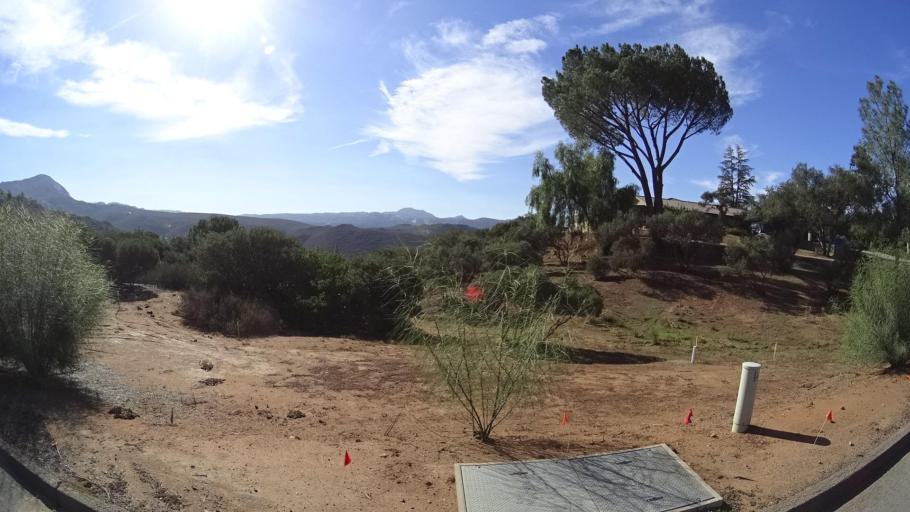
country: US
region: California
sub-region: San Diego County
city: Alpine
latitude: 32.8221
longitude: -116.7436
